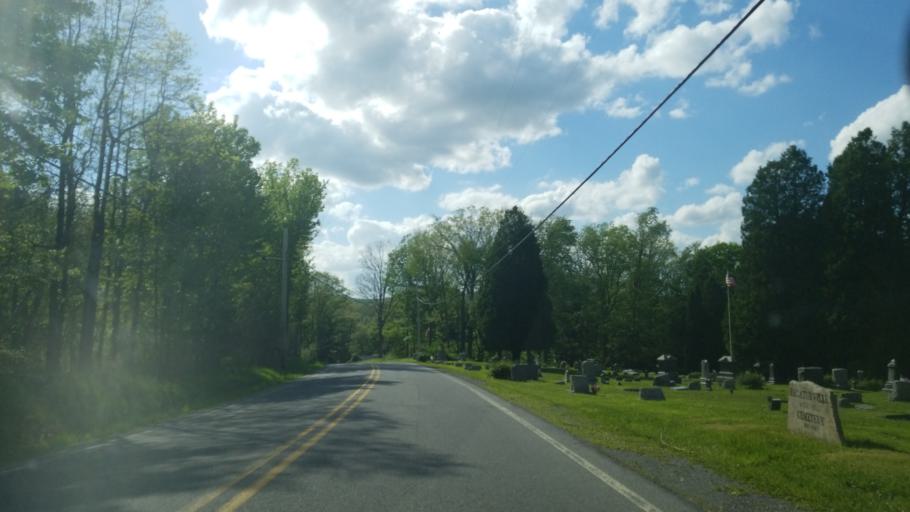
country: US
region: Pennsylvania
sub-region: Clearfield County
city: Troy
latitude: 40.9209
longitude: -78.2688
